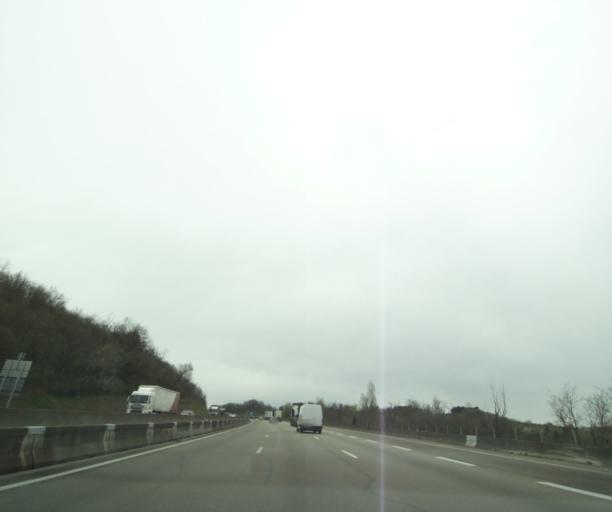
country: FR
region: Rhone-Alpes
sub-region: Departement de la Drome
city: Saint-Barthelemy-de-Vals
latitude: 45.1485
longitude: 4.8881
